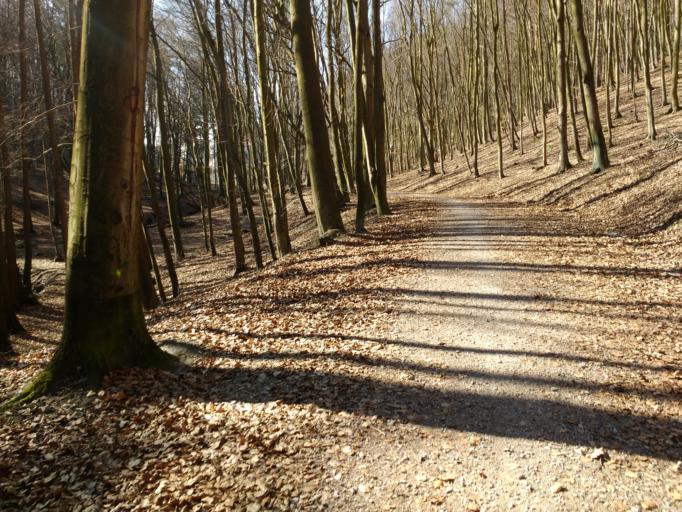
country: PL
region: Pomeranian Voivodeship
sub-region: Gdynia
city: Wielki Kack
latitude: 54.4797
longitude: 18.5139
